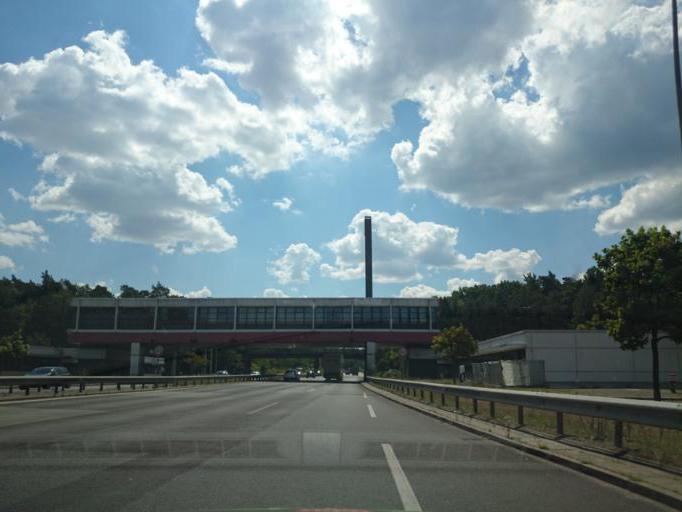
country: DE
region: Berlin
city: Nikolassee
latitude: 52.4170
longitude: 13.1966
